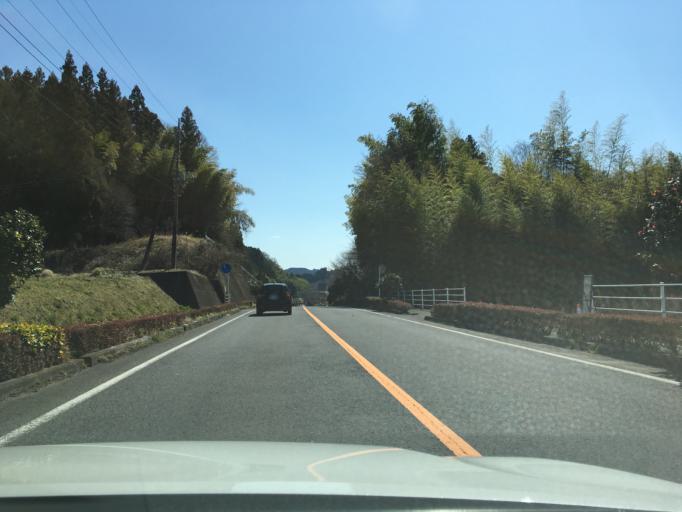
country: JP
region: Tochigi
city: Kuroiso
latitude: 37.0389
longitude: 140.1716
